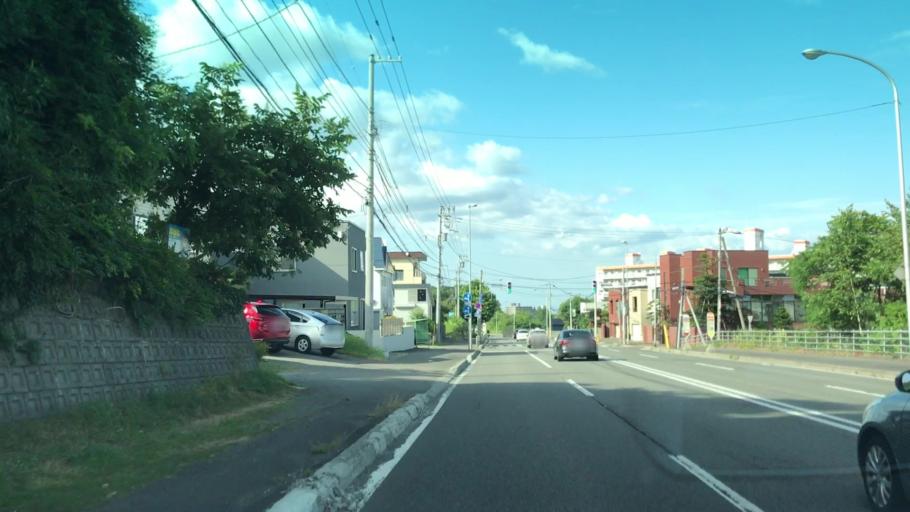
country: JP
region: Hokkaido
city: Sapporo
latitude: 42.9813
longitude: 141.3463
